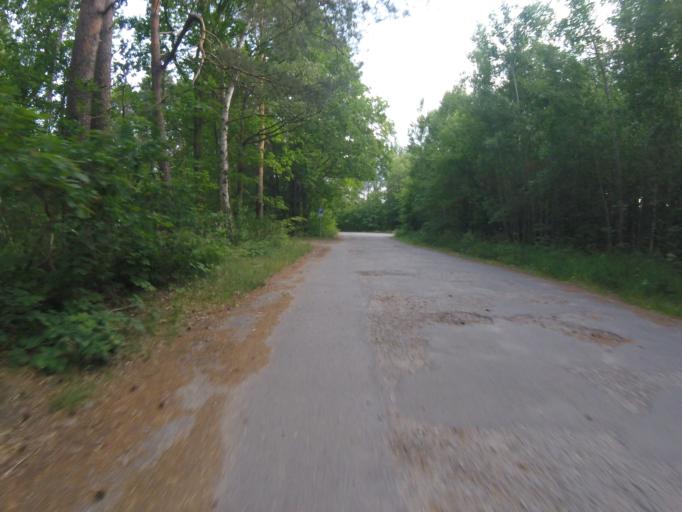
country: DE
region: Brandenburg
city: Konigs Wusterhausen
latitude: 52.3029
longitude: 13.6157
